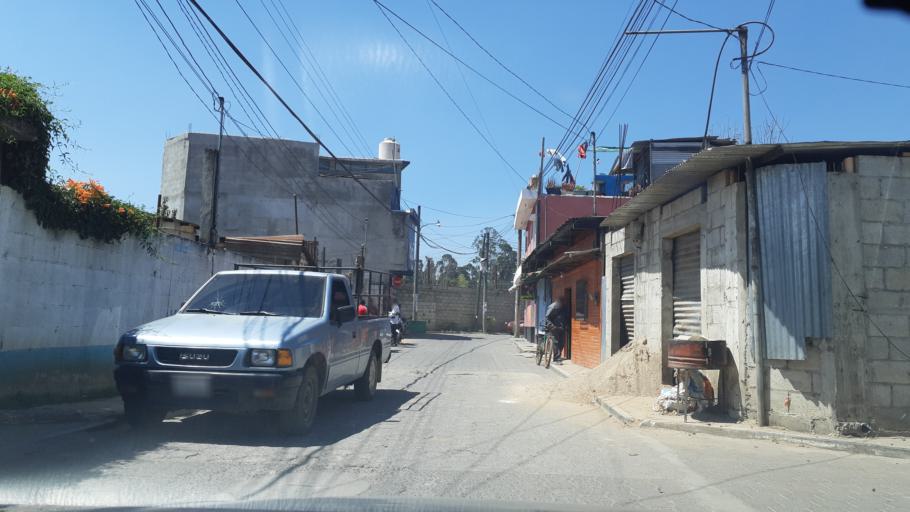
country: GT
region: Chimaltenango
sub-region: Municipio de Chimaltenango
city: Chimaltenango
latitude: 14.6521
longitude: -90.8127
